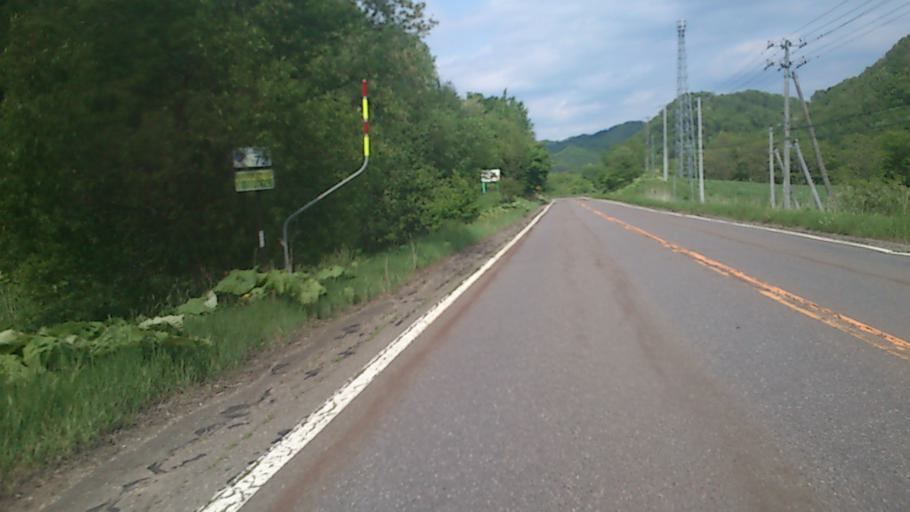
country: JP
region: Hokkaido
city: Kitami
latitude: 43.3459
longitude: 143.7728
